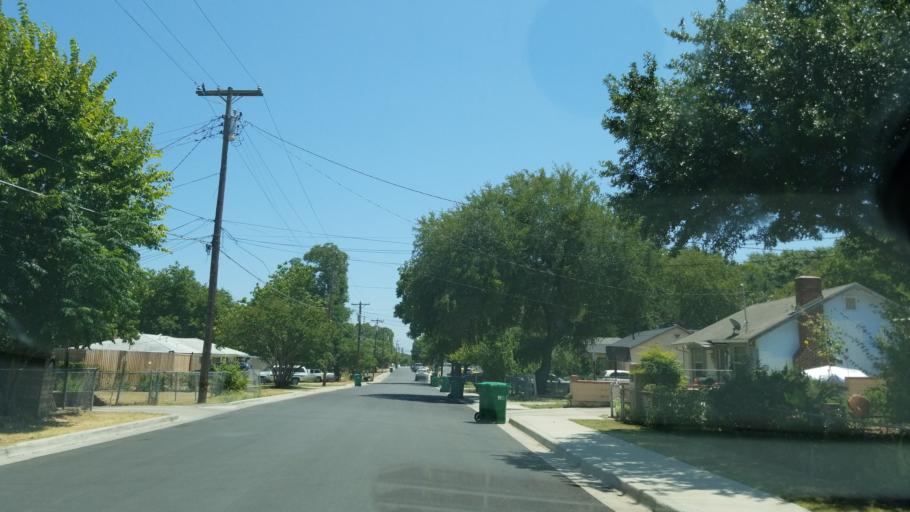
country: US
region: Texas
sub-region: Dallas County
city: Cockrell Hill
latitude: 32.7365
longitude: -96.8866
